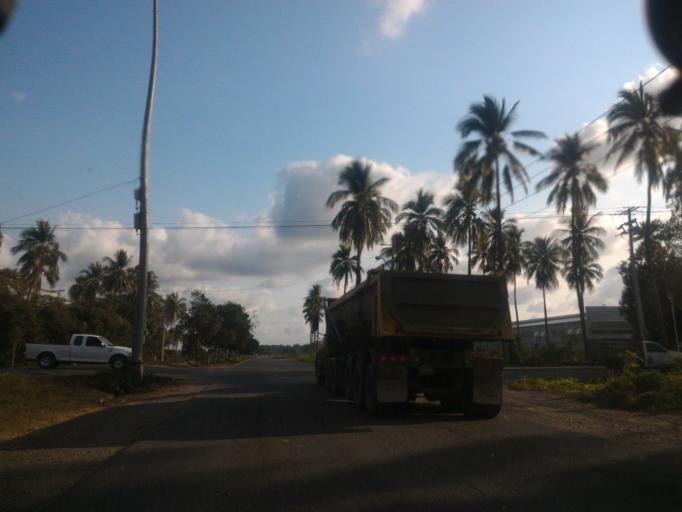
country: MX
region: Colima
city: Tecoman
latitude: 18.9187
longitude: -103.8542
